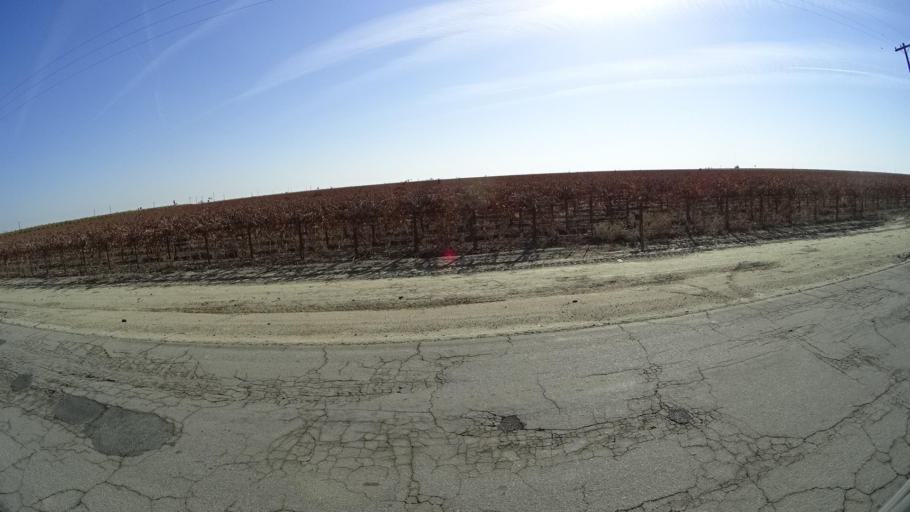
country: US
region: California
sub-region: Kern County
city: Wasco
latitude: 35.7031
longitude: -119.3865
